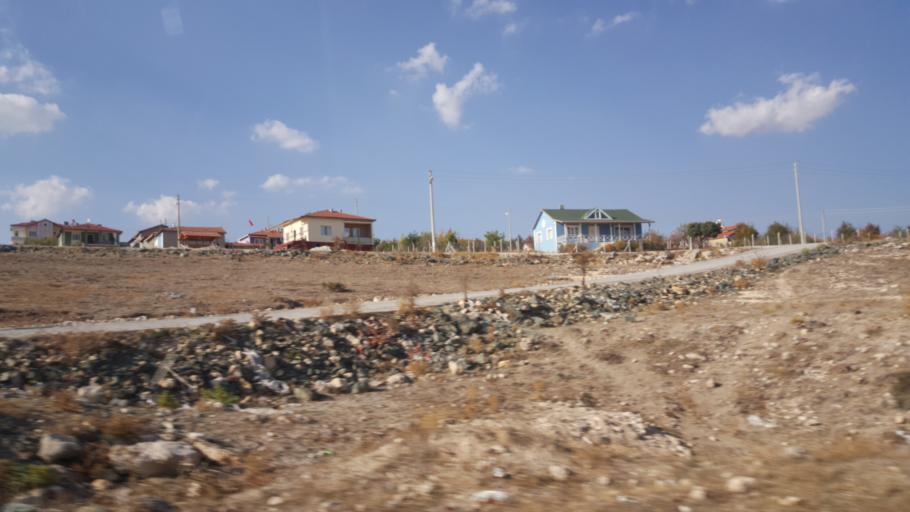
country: TR
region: Eskisehir
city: Kirka
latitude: 39.3242
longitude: 30.5621
